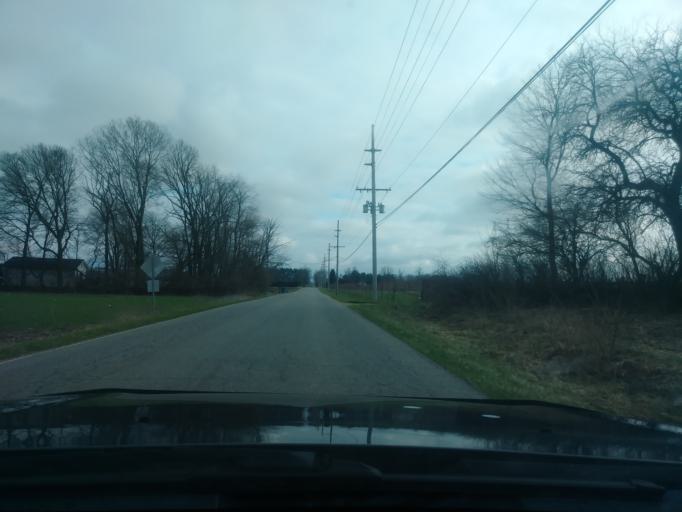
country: US
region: Indiana
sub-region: LaPorte County
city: LaPorte
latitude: 41.6053
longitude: -86.7978
